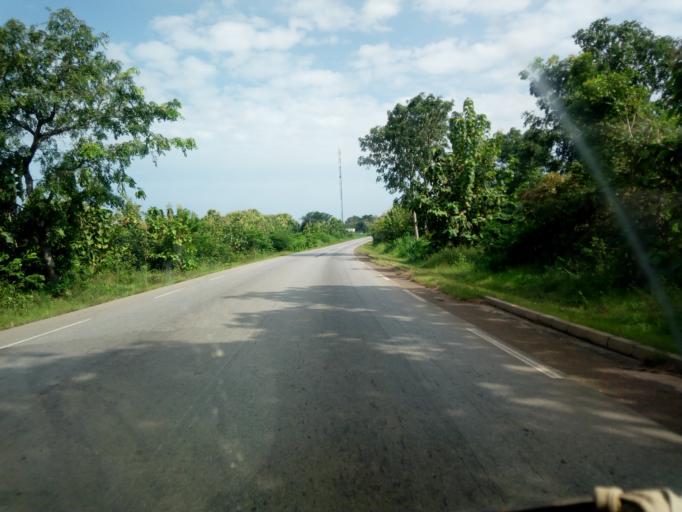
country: TG
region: Plateaux
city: Notse
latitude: 7.0557
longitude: 1.1532
